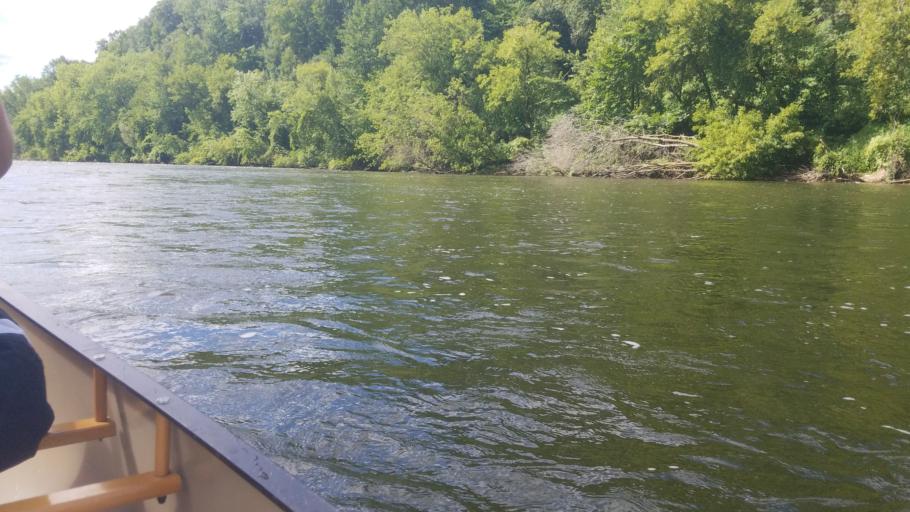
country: US
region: Wisconsin
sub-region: Dunn County
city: Menomonie
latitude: 44.8583
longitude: -91.9493
